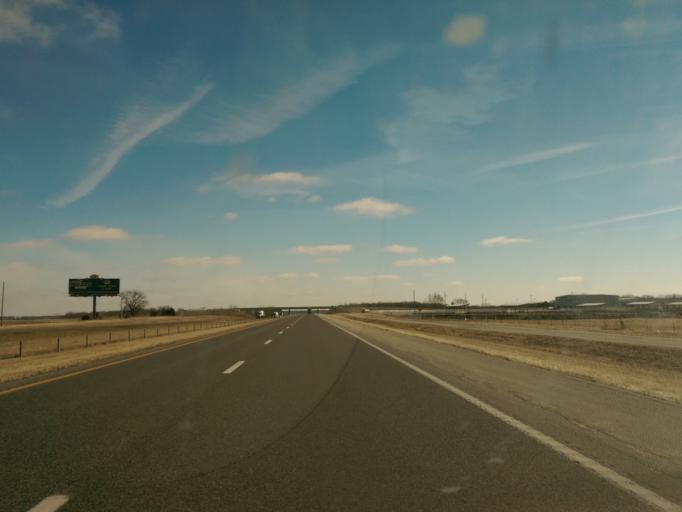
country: US
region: Missouri
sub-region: Callaway County
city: Fulton
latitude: 38.9408
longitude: -91.8705
